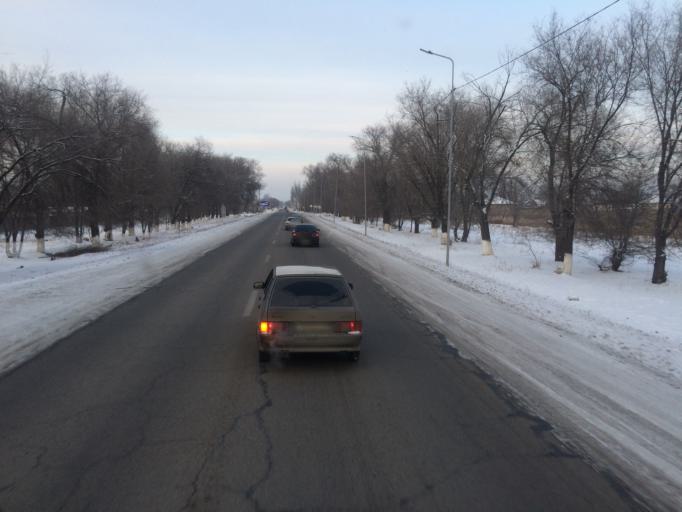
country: KZ
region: Almaty Oblysy
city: Burunday
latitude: 43.2645
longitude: 76.6699
